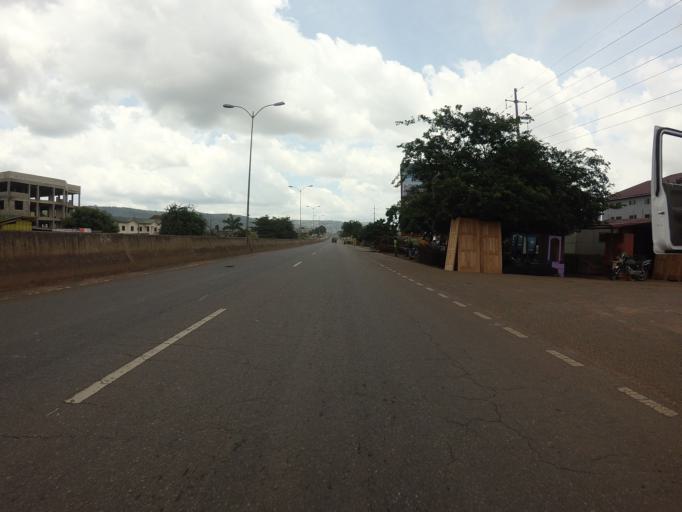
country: GH
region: Greater Accra
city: Medina Estates
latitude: 5.7546
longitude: -0.1784
